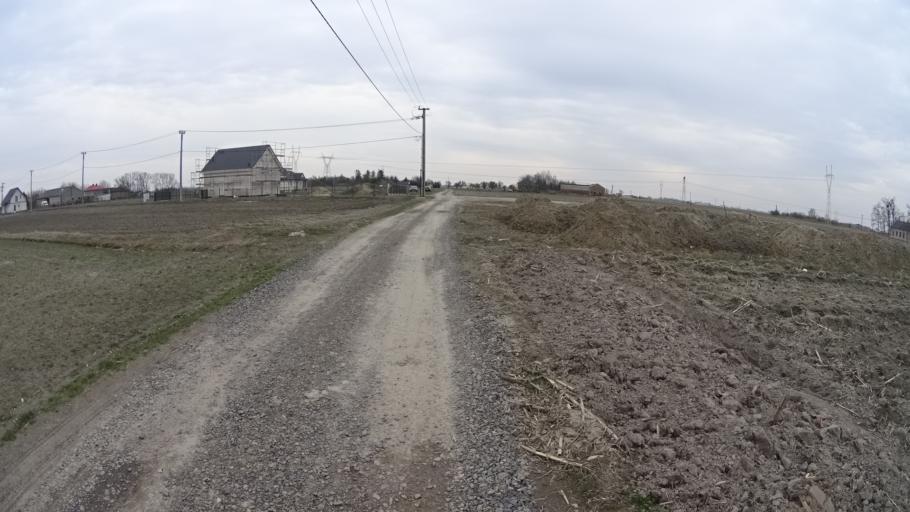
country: PL
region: Masovian Voivodeship
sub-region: Powiat warszawski zachodni
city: Jozefow
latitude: 52.2419
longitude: 20.6887
